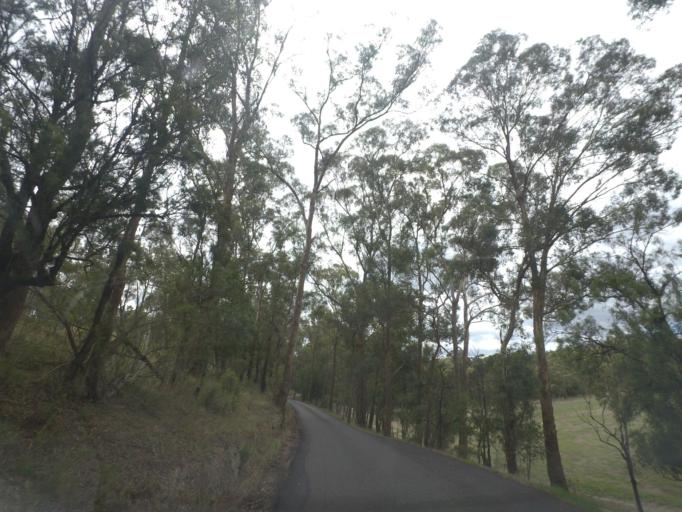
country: AU
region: Victoria
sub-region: Manningham
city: Park Orchards
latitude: -37.7797
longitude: 145.1982
